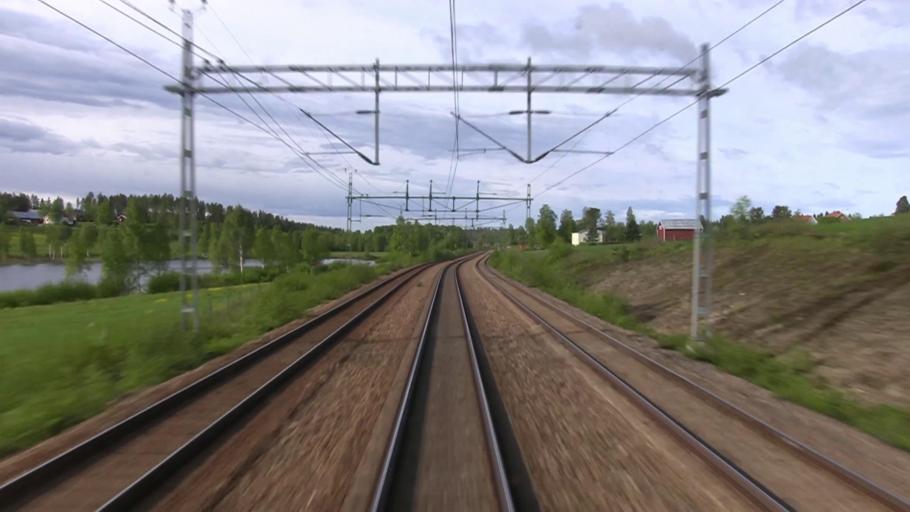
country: SE
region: Vaesterbotten
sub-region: Vindelns Kommun
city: Vindeln
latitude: 64.1012
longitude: 19.6794
